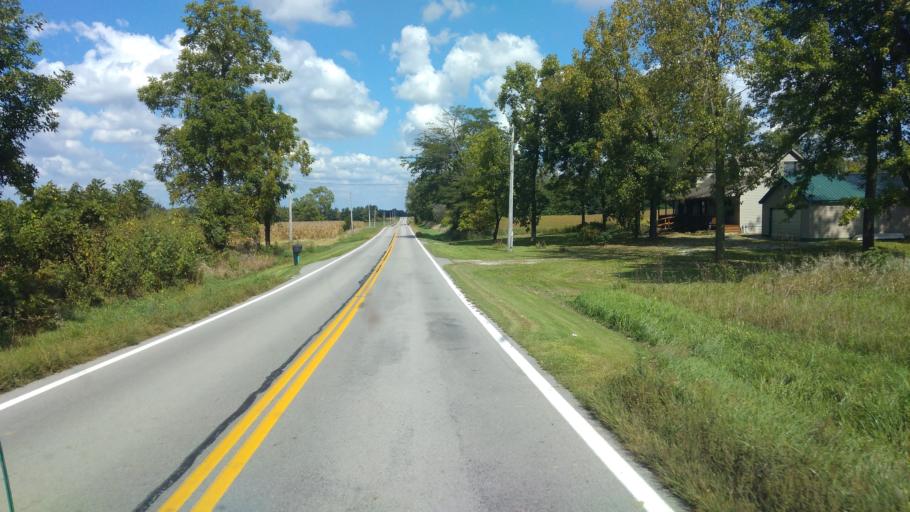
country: US
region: Ohio
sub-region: Hardin County
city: Forest
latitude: 40.6630
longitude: -83.3811
